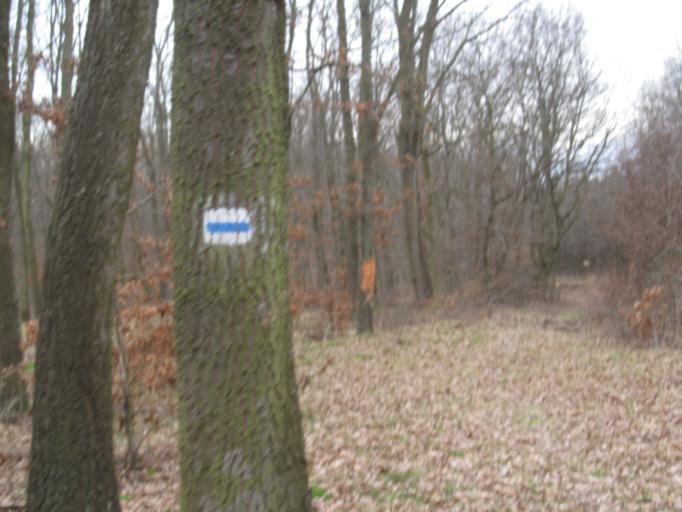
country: HU
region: Vas
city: Sarvar
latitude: 47.2409
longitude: 17.0036
